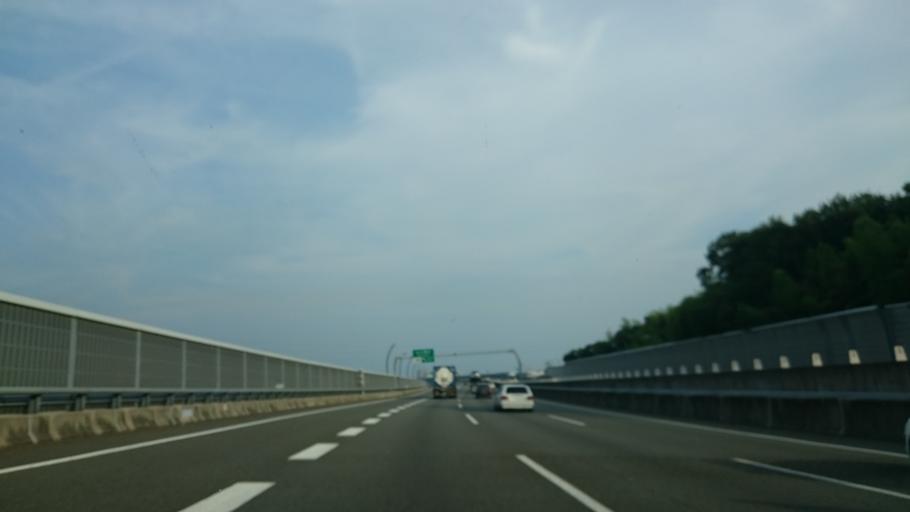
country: JP
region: Mie
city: Yokkaichi
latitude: 35.0333
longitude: 136.6434
